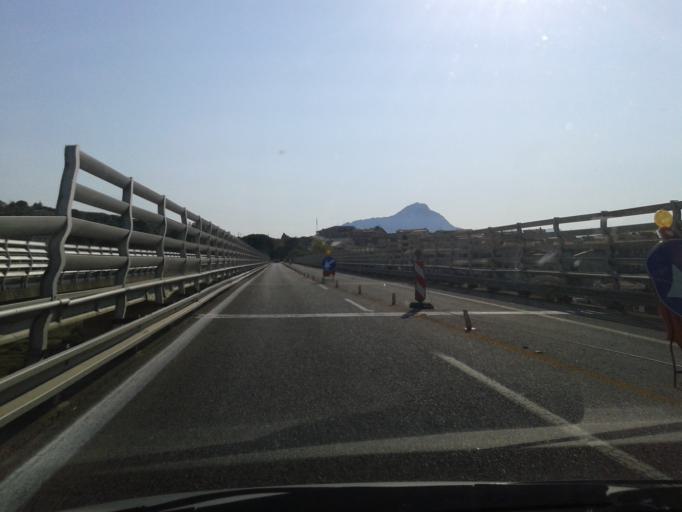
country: IT
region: Sicily
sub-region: Palermo
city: Campofelice di Roccella
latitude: 37.9873
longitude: 13.8905
